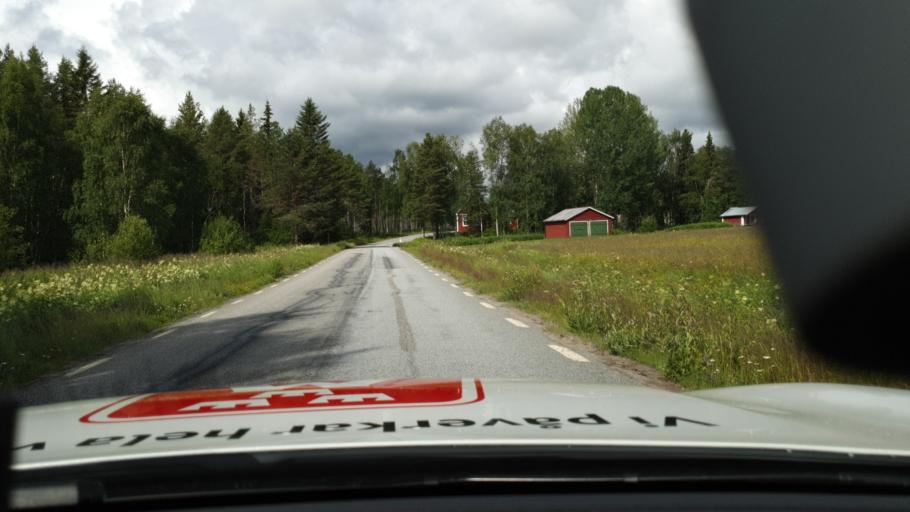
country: SE
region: Norrbotten
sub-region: Pitea Kommun
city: Rosvik
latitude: 65.4221
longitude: 21.8474
